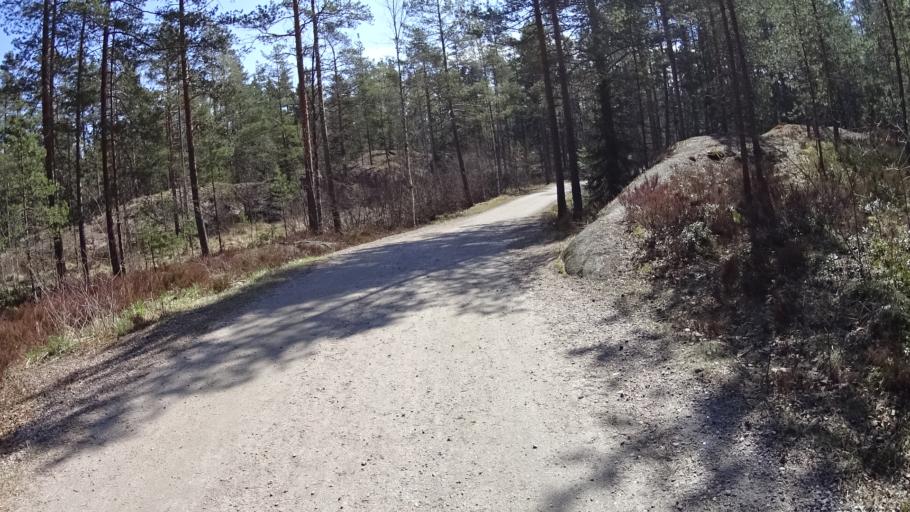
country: FI
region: Uusimaa
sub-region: Helsinki
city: Espoo
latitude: 60.2693
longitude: 24.6401
